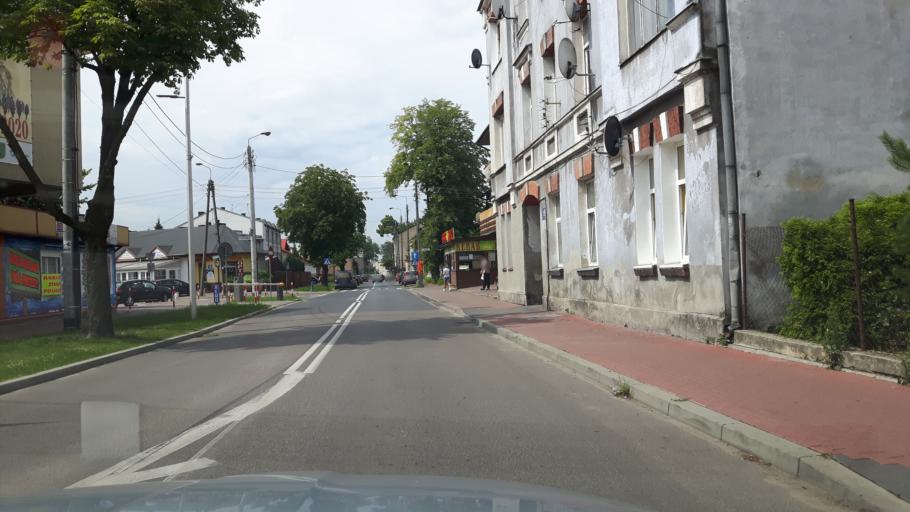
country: PL
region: Masovian Voivodeship
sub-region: Powiat wolominski
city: Wolomin
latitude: 52.3449
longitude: 21.2387
